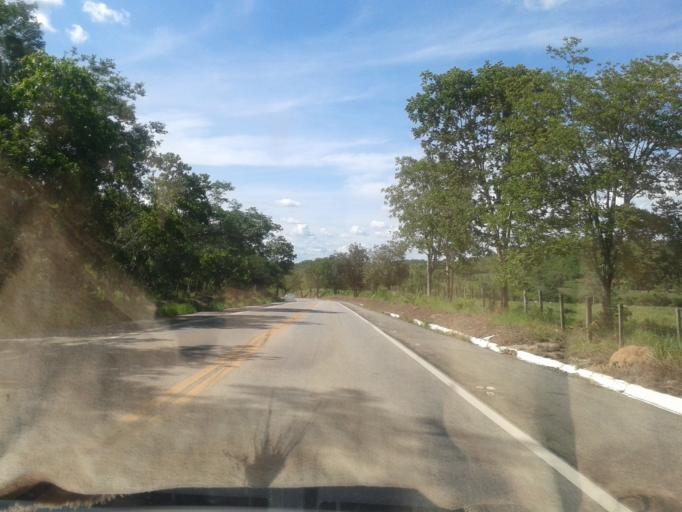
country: BR
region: Goias
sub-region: Itapuranga
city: Itapuranga
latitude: -15.3928
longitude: -50.3865
